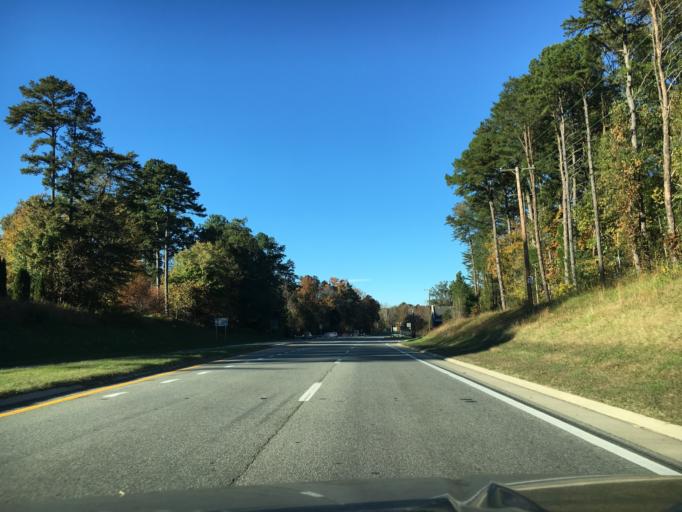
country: US
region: Virginia
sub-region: Halifax County
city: South Boston
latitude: 36.7008
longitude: -78.8886
